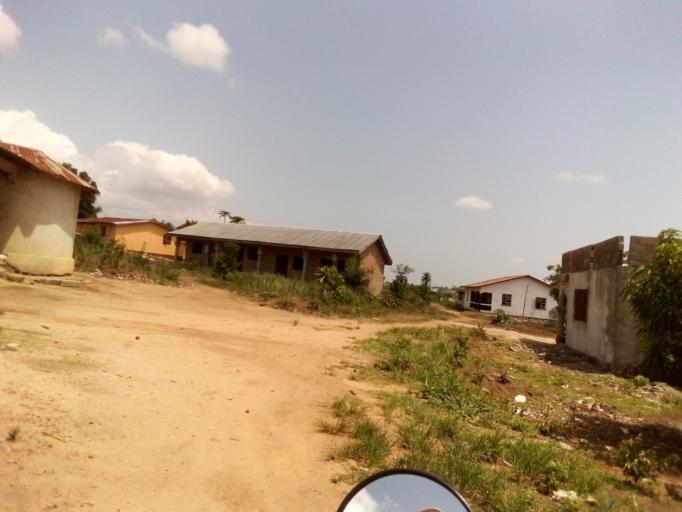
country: SL
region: Western Area
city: Waterloo
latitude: 8.3430
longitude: -13.0249
